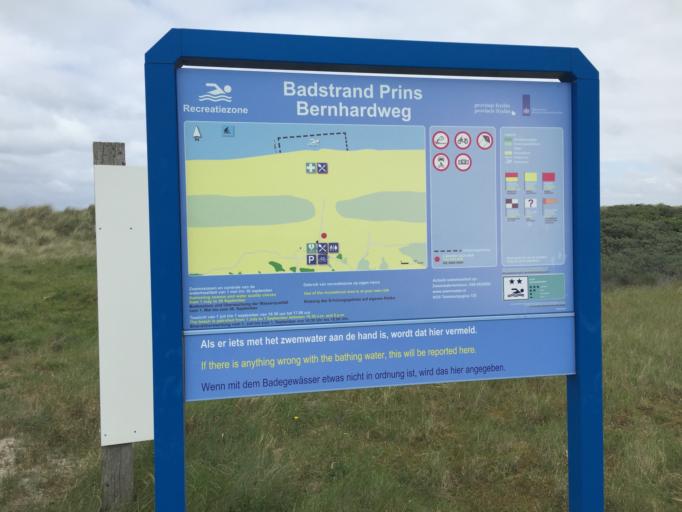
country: NL
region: Friesland
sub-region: Gemeente Schiermonnikoog
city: Schiermonnikoog
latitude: 53.4979
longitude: 6.1888
